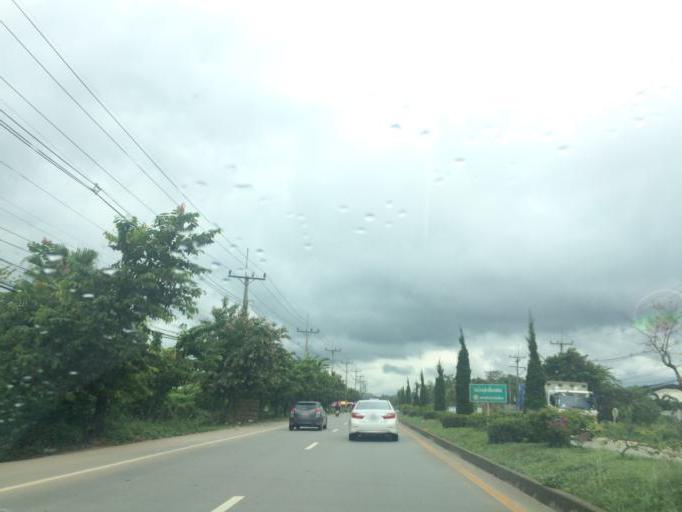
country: TH
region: Chiang Rai
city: Mae Chan
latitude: 20.0266
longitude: 99.8727
